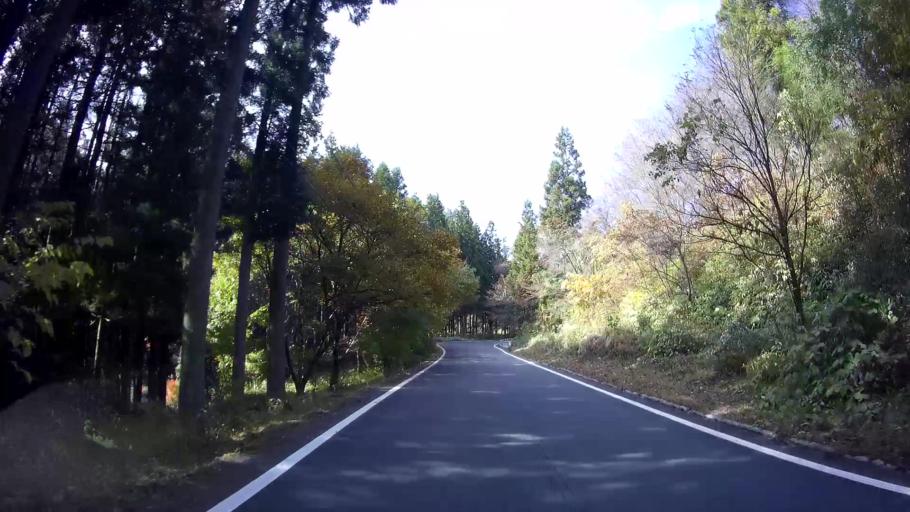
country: JP
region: Gunma
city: Nakanojomachi
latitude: 36.5026
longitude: 138.6815
